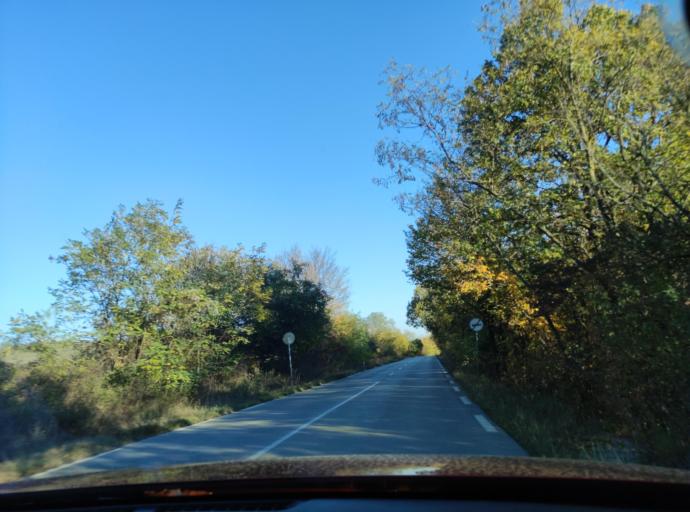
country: BG
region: Montana
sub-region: Obshtina Chiprovtsi
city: Chiprovtsi
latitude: 43.4318
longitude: 22.9903
